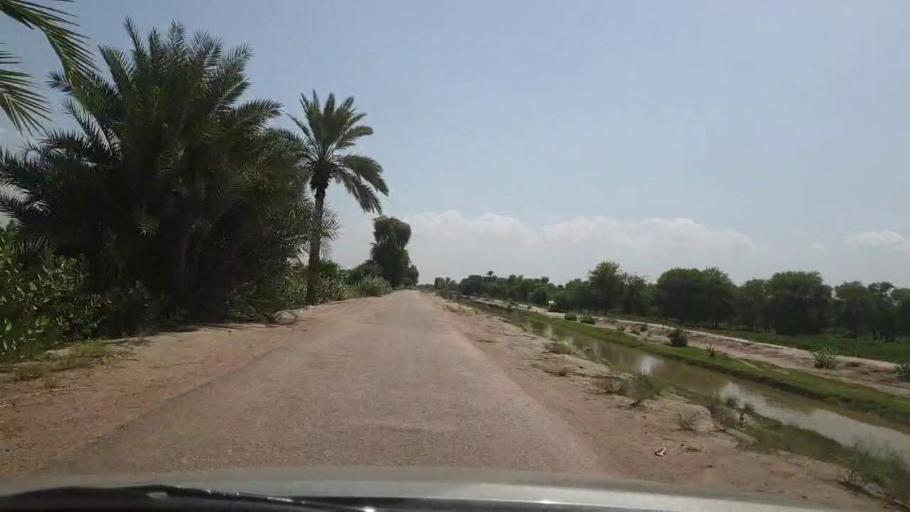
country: PK
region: Sindh
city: Pano Aqil
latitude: 27.7307
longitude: 69.0933
